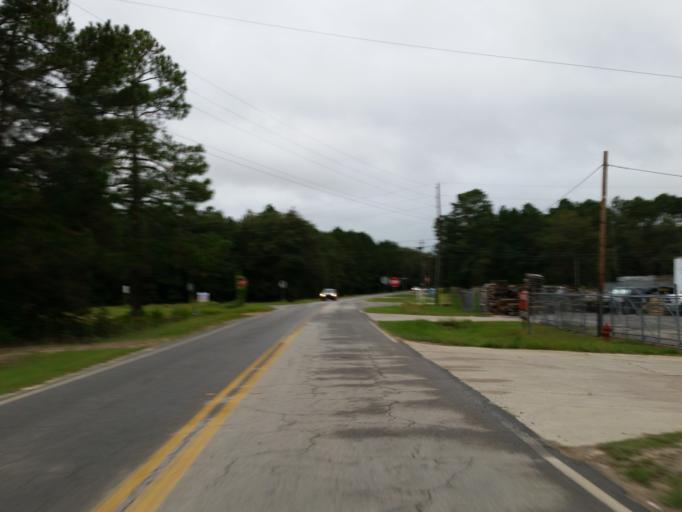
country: US
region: Georgia
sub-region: Turner County
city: Ashburn
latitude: 31.6848
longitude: -83.6397
